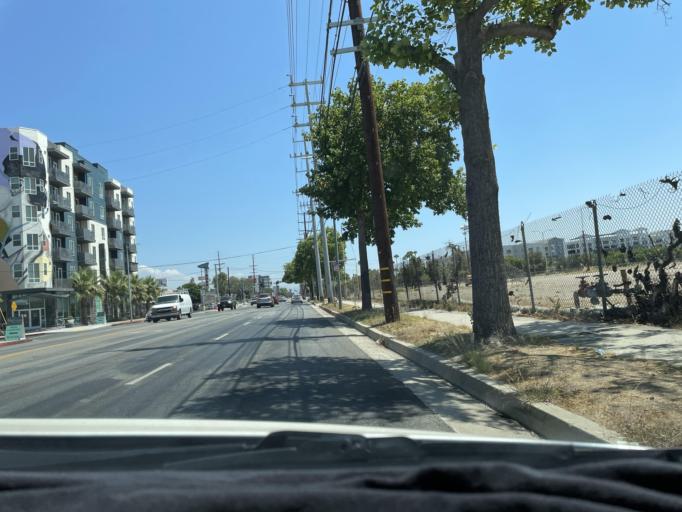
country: US
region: California
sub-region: Los Angeles County
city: Canoga Park
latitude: 34.1937
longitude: -118.5996
